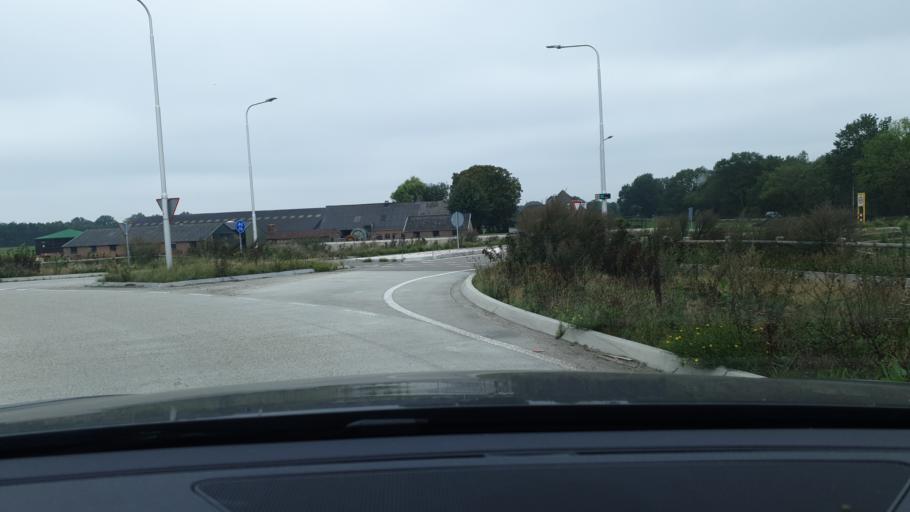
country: NL
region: North Brabant
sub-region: Gemeente Landerd
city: Schaijk
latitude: 51.7339
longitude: 5.5996
